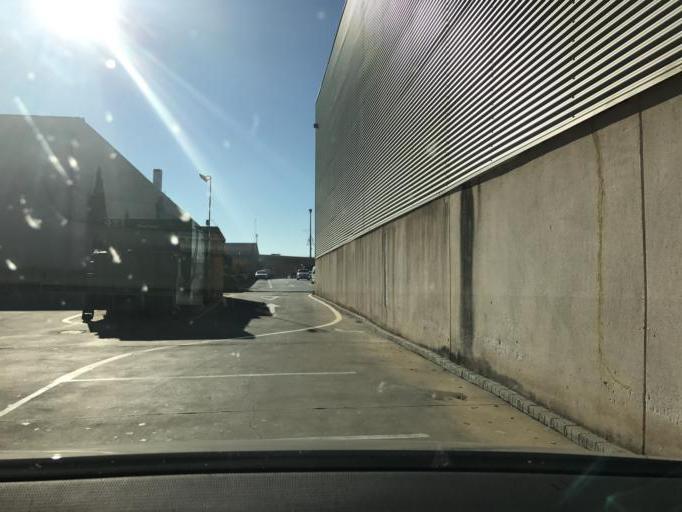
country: ES
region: Andalusia
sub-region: Provincia de Granada
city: Pulianas
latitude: 37.2155
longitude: -3.6182
